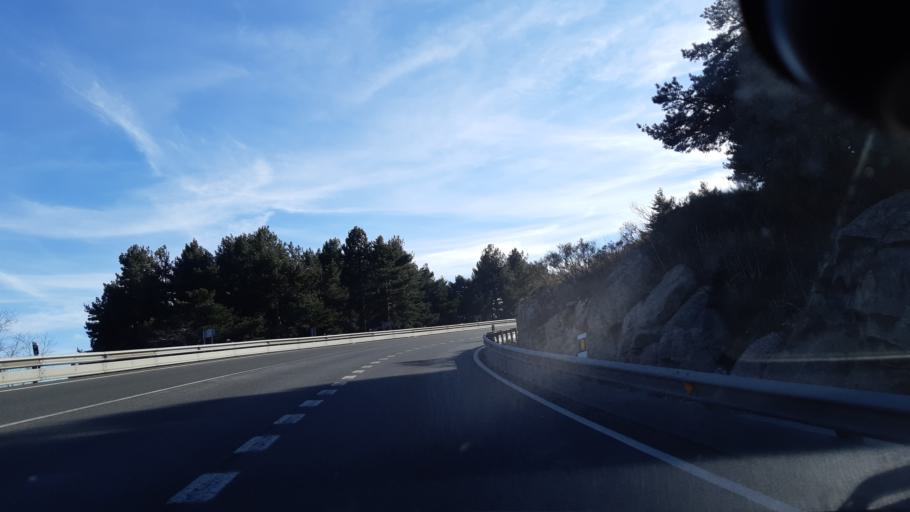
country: ES
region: Madrid
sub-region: Provincia de Madrid
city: Guadarrama
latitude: 40.7079
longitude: -4.1288
